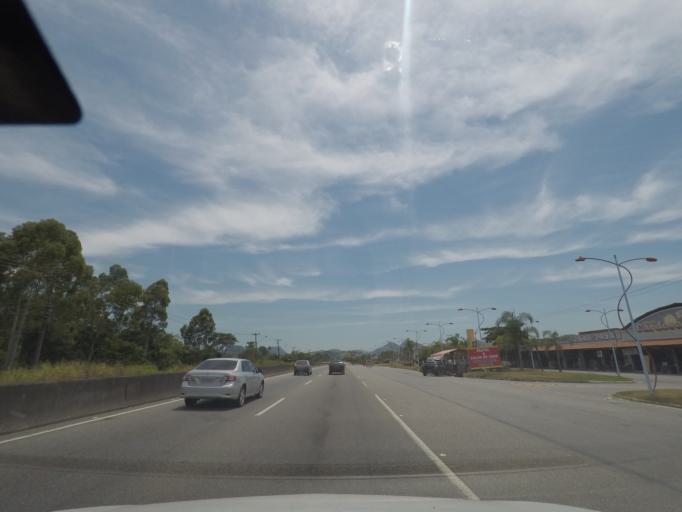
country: BR
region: Rio de Janeiro
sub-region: Marica
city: Marica
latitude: -22.9174
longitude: -42.8515
